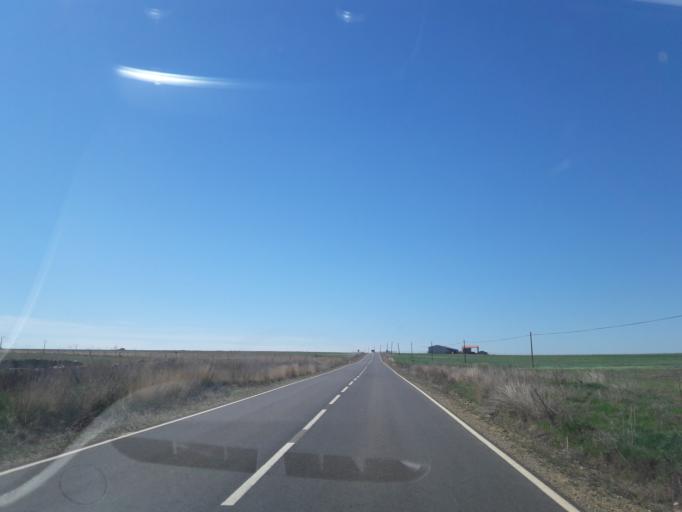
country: ES
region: Castille and Leon
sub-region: Provincia de Salamanca
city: Valdemierque
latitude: 40.8147
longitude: -5.5911
